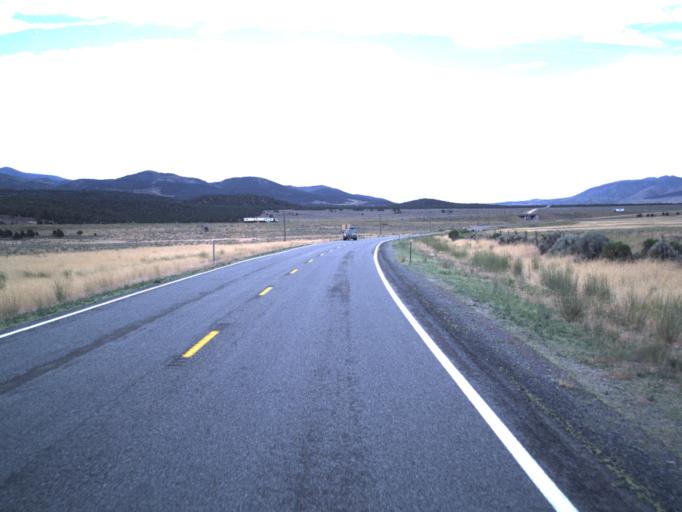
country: US
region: Utah
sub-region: Beaver County
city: Beaver
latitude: 38.5956
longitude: -112.5814
